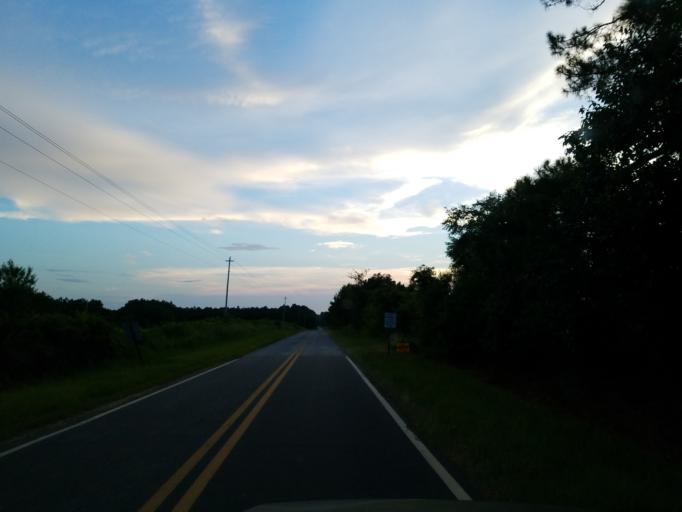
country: US
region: Georgia
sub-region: Crisp County
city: Cordele
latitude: 31.8377
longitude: -83.7544
